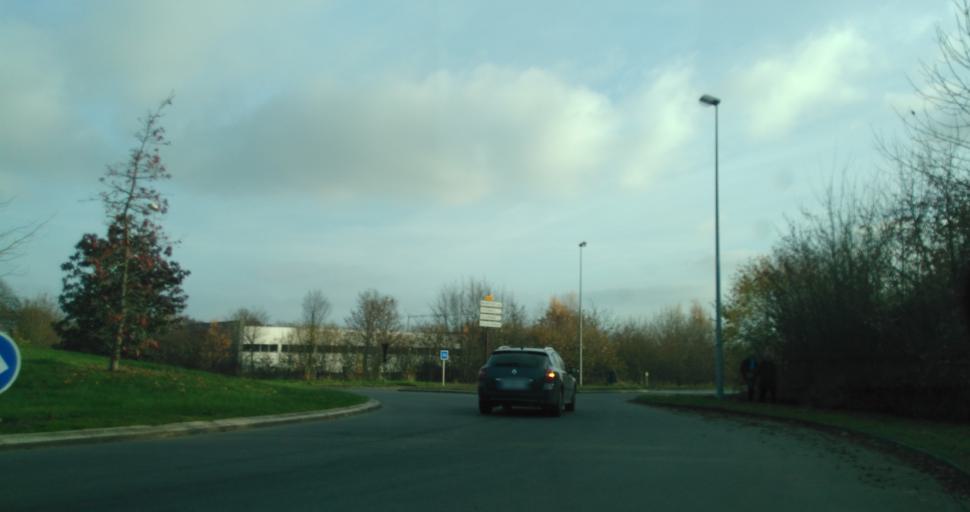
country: FR
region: Brittany
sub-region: Departement d'Ille-et-Vilaine
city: Montfort-sur-Meu
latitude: 48.1382
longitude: -1.9372
